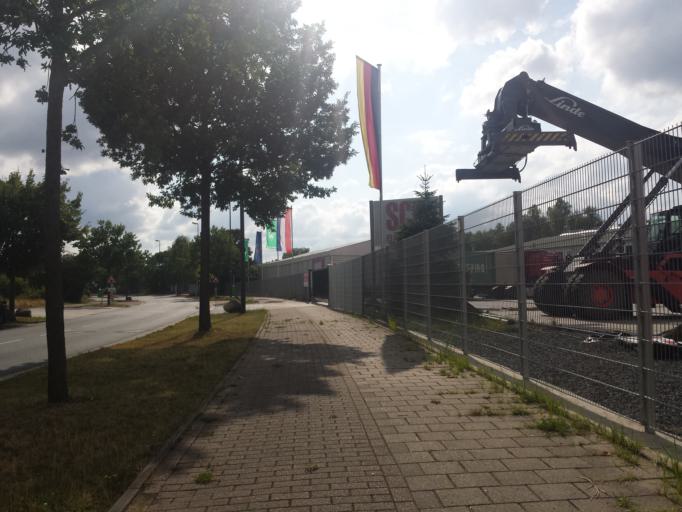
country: DE
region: Lower Saxony
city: Stuhr
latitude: 53.0941
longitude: 8.7082
